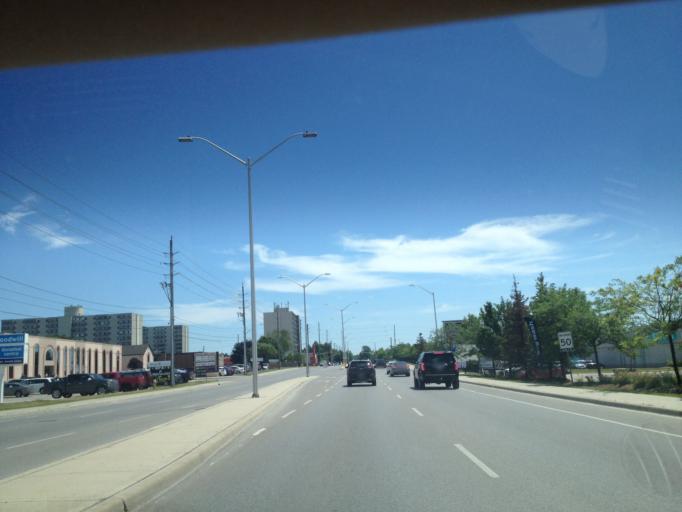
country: CA
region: Ontario
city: London
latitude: 42.9782
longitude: -81.3217
